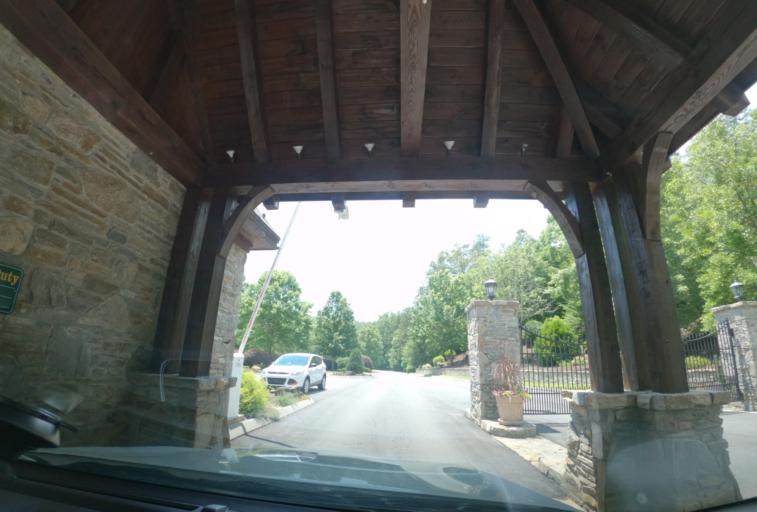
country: US
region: South Carolina
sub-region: Pickens County
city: Pickens
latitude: 34.9611
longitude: -82.8694
